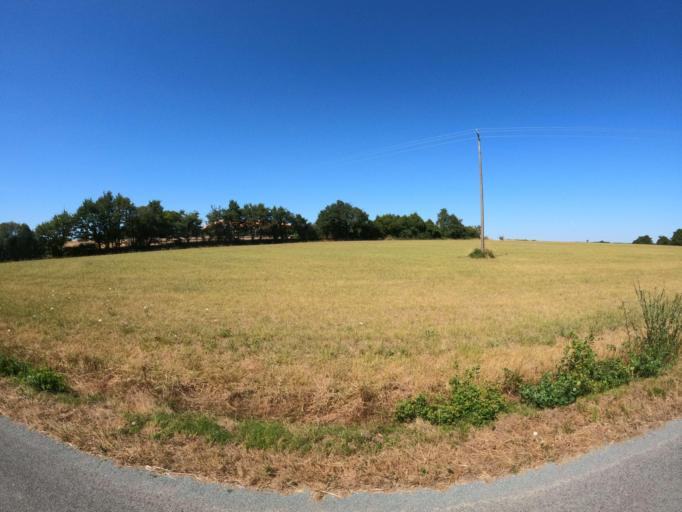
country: FR
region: Pays de la Loire
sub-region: Departement de Maine-et-Loire
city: Saint-Christophe-du-Bois
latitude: 47.0481
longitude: -0.9618
